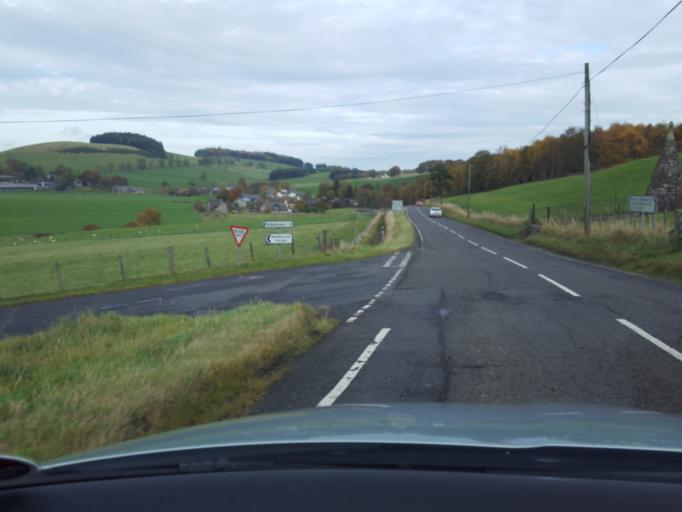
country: GB
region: Scotland
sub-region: The Scottish Borders
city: West Linton
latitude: 55.6894
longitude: -3.3892
